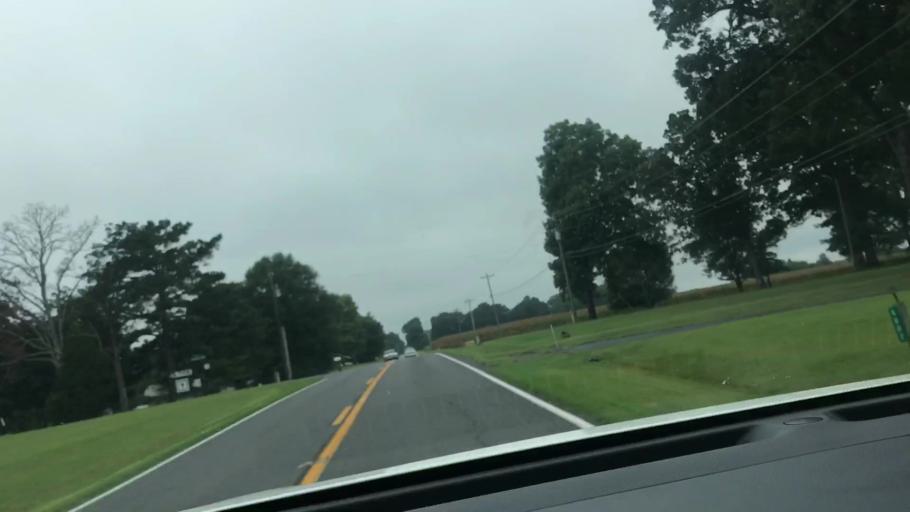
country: US
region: Kentucky
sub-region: Calloway County
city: Murray
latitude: 36.5806
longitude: -88.2584
